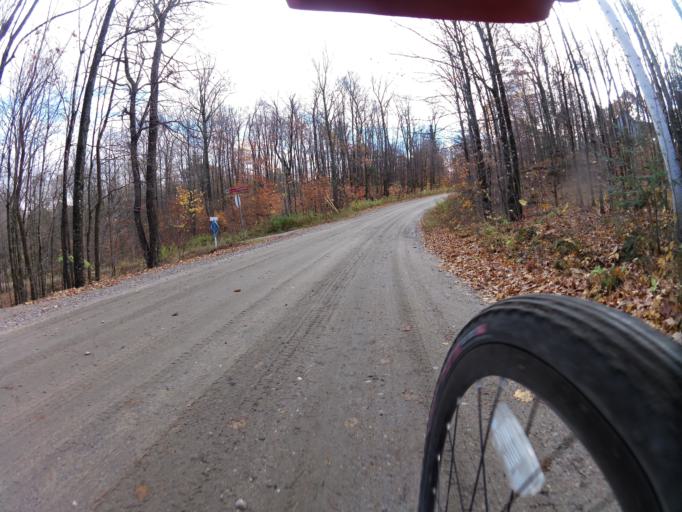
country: CA
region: Quebec
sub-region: Outaouais
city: Wakefield
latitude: 45.7274
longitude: -76.0293
